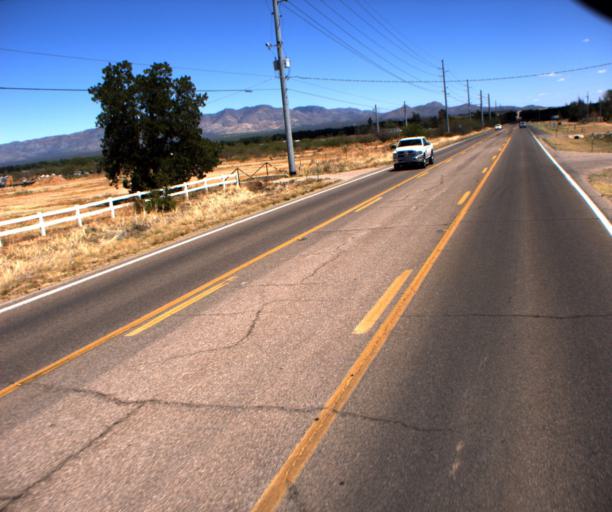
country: US
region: Arizona
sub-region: Cochise County
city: Sierra Vista Southeast
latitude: 31.3799
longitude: -110.1220
